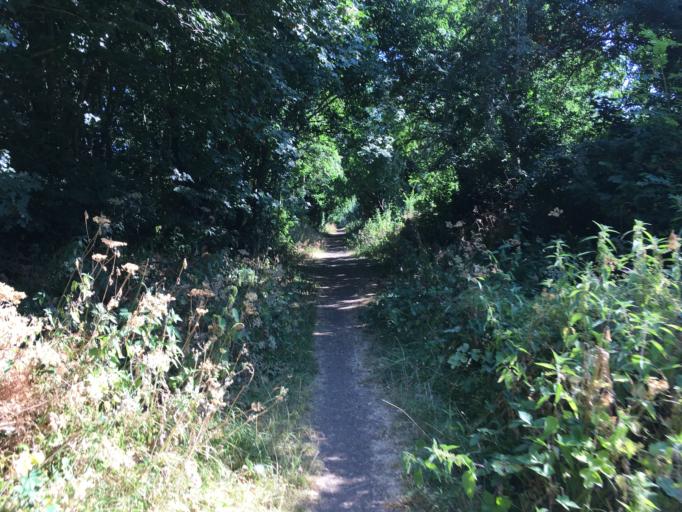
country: GB
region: England
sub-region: Warwickshire
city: Rugby
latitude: 52.3899
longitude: -1.2374
